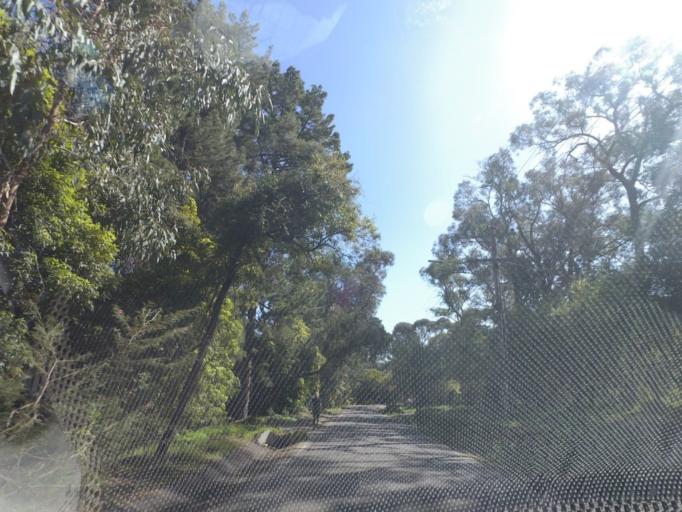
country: AU
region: Victoria
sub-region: Manningham
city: Park Orchards
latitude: -37.7892
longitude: 145.2275
